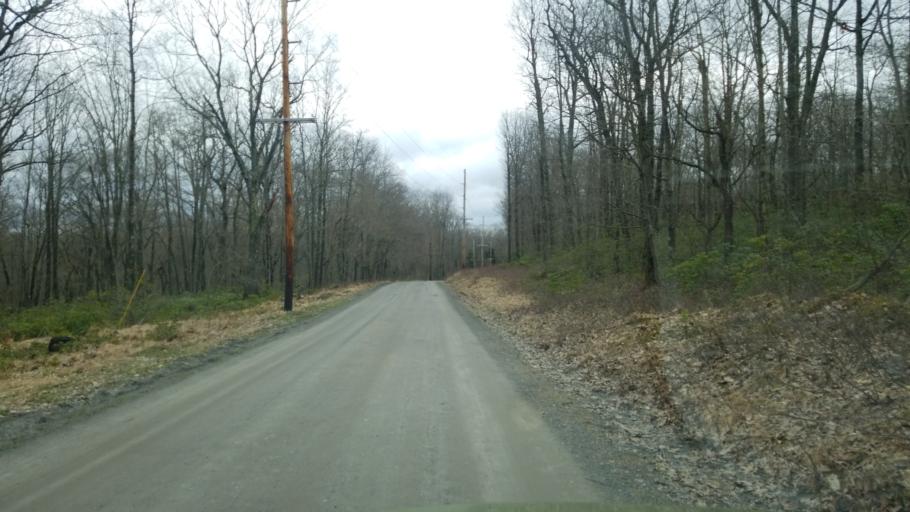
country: US
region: Pennsylvania
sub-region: Clearfield County
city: Shiloh
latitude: 41.1715
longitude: -78.2927
